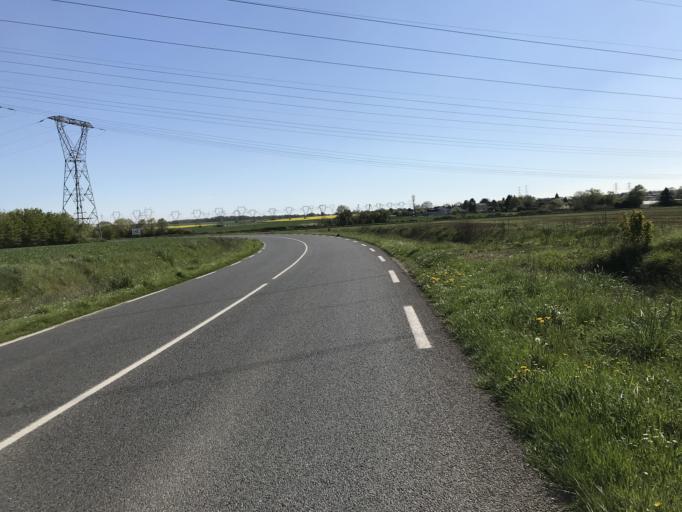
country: FR
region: Ile-de-France
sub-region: Departement de l'Essonne
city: Villejust
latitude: 48.6790
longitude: 2.2254
